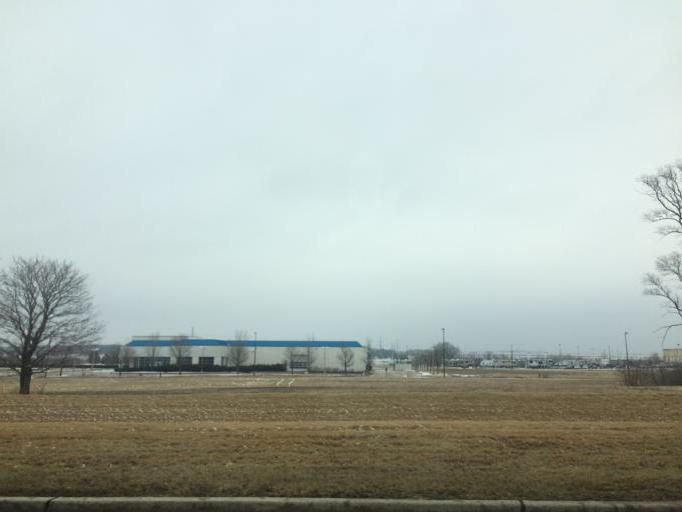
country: US
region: Illinois
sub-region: McHenry County
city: Huntley
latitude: 42.1251
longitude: -88.4326
